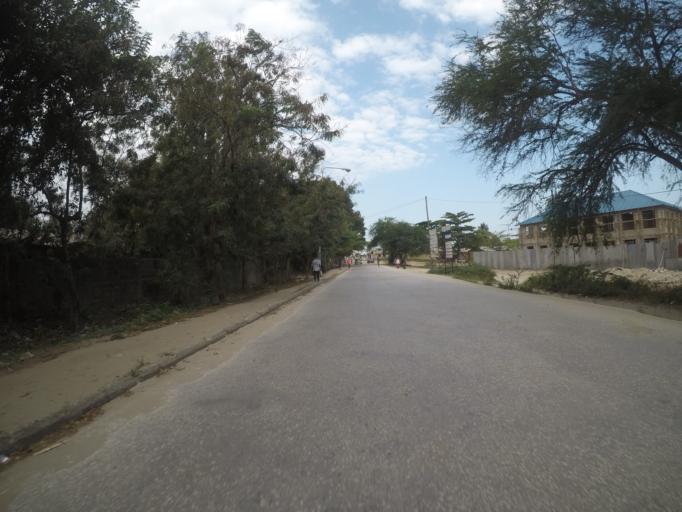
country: TZ
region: Zanzibar Urban/West
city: Zanzibar
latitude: -6.1748
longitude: 39.2059
